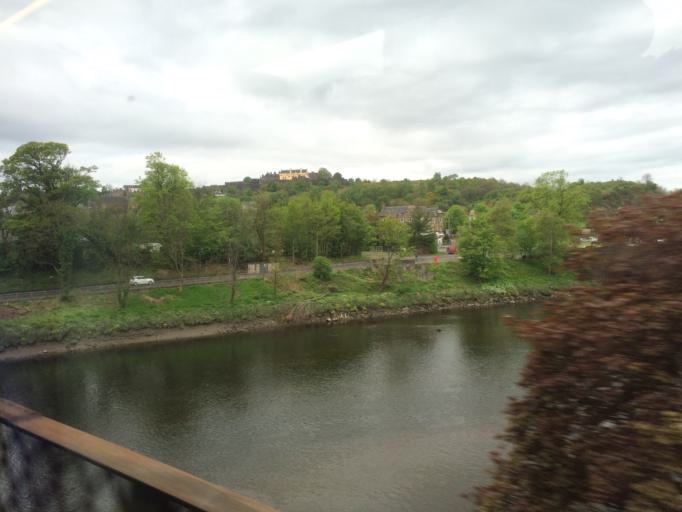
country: GB
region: Scotland
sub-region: Stirling
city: Stirling
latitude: 56.1273
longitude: -3.9348
